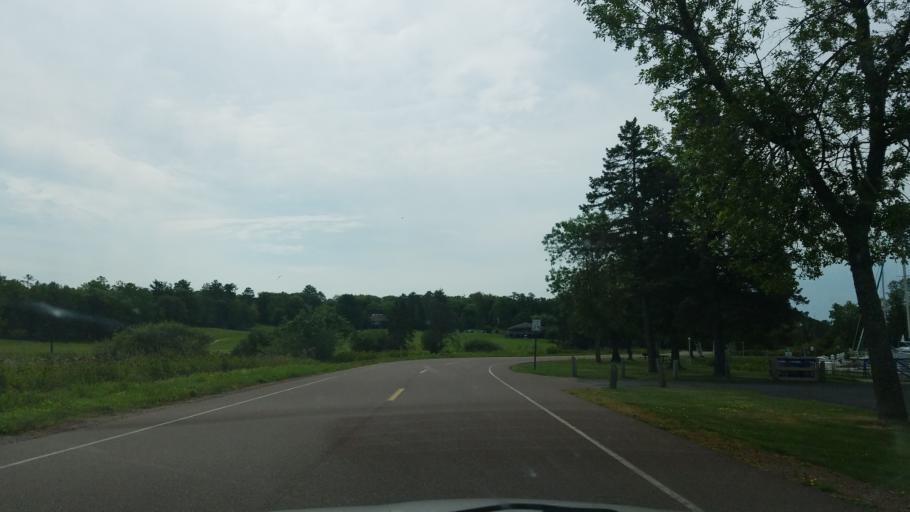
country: US
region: Wisconsin
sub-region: Bayfield County
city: Washburn
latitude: 46.7722
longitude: -90.7794
